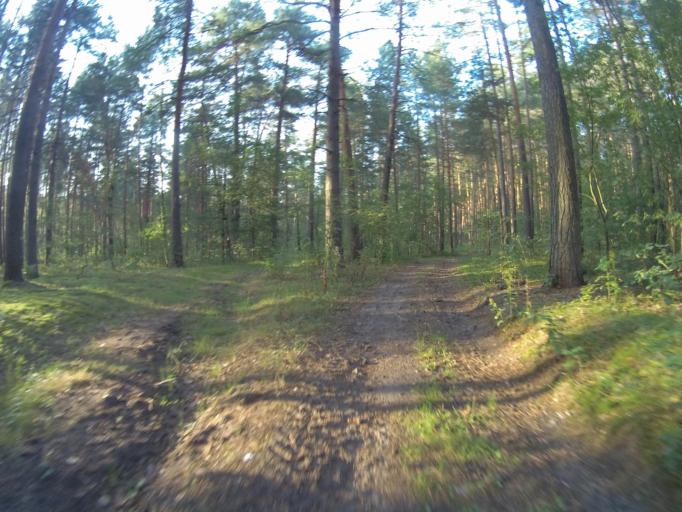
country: RU
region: Vladimir
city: Kommunar
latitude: 56.0728
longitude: 40.4339
